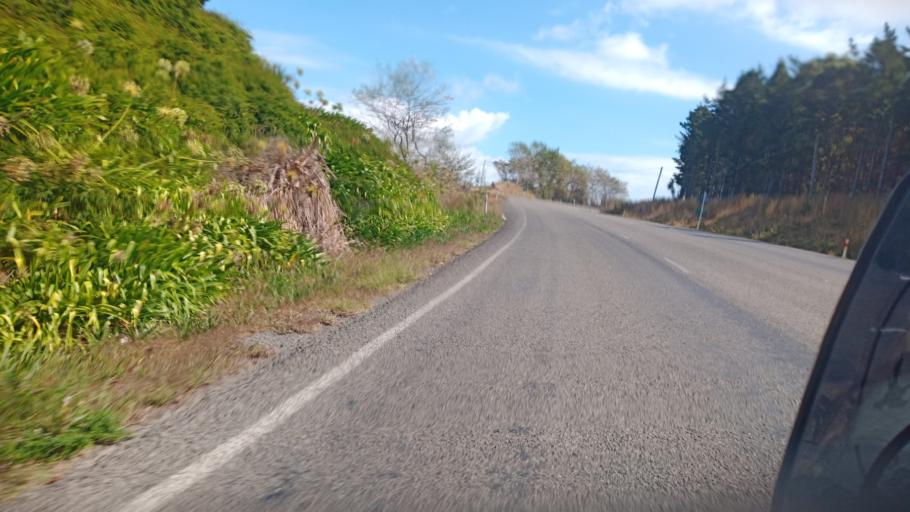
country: NZ
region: Gisborne
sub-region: Gisborne District
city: Gisborne
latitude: -38.5342
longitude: 178.2234
